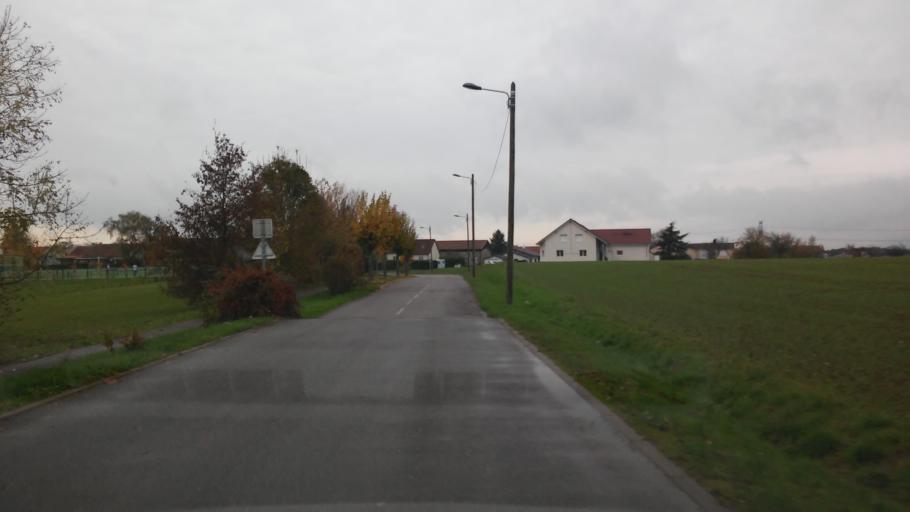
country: FR
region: Lorraine
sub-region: Departement de la Moselle
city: Vigy
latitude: 49.1869
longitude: 6.3319
